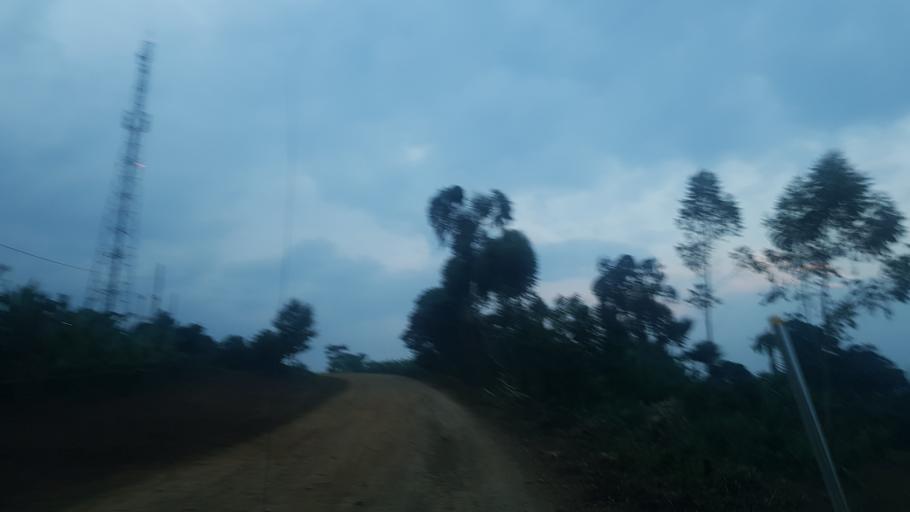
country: ET
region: Oromiya
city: Gore
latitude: 7.7851
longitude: 35.4599
